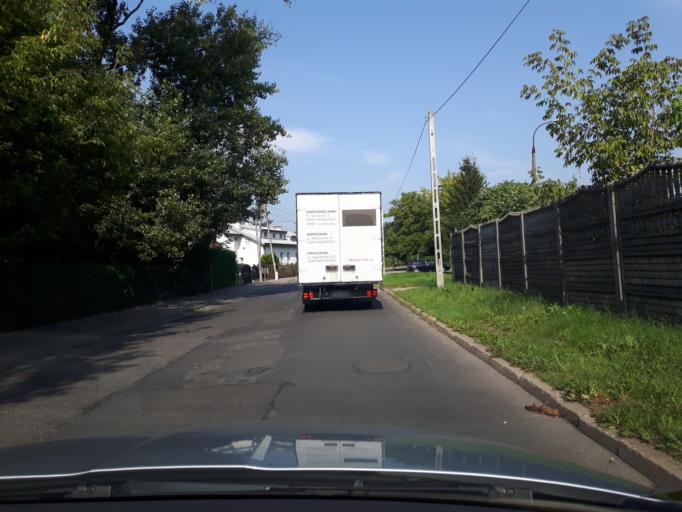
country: PL
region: Masovian Voivodeship
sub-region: Warszawa
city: Targowek
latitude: 52.2765
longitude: 21.0740
